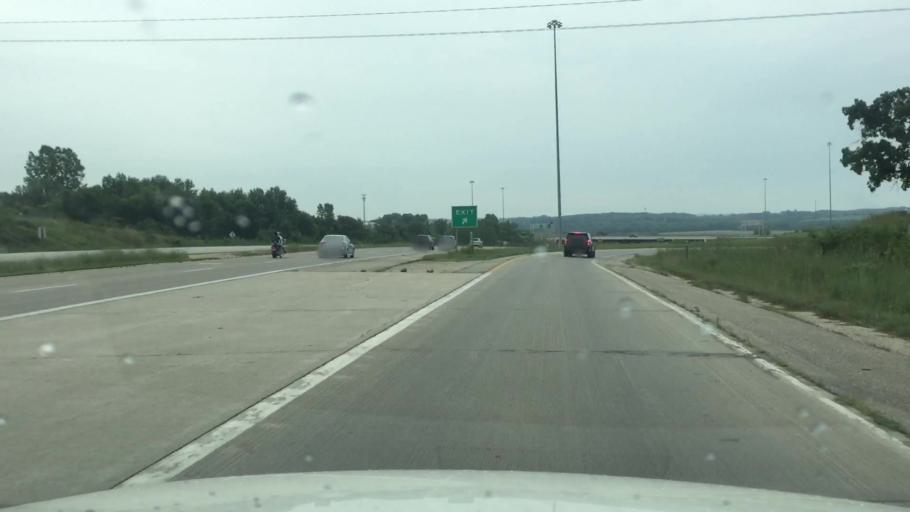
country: US
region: Iowa
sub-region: Warren County
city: Carlisle
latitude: 41.5098
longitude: -93.5755
